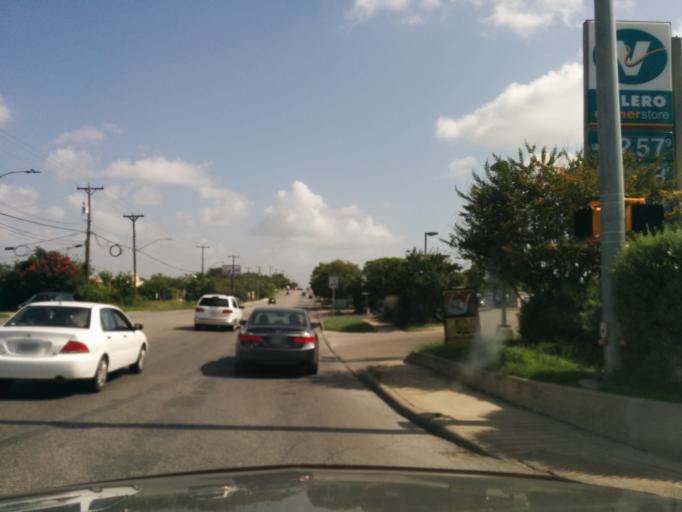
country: US
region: Texas
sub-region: Bexar County
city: Leon Valley
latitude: 29.5446
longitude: -98.6148
